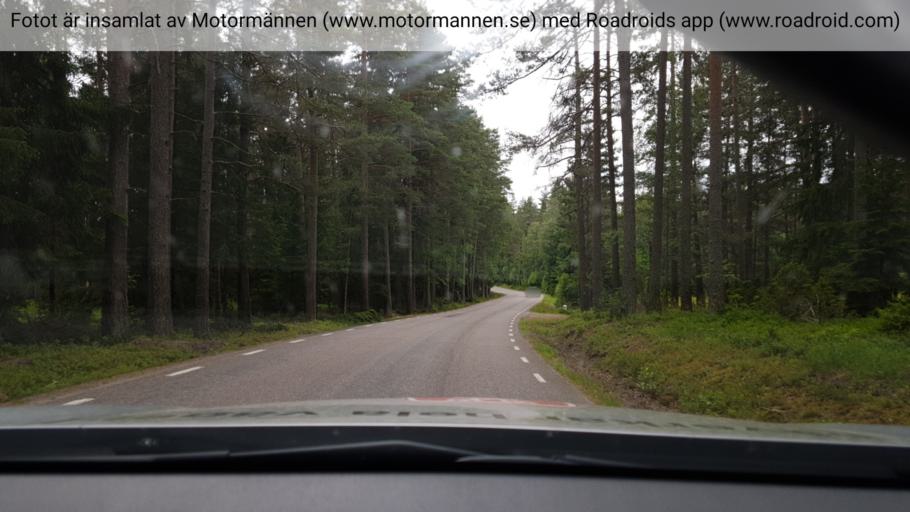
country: SE
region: Joenkoeping
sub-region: Habo Kommun
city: Habo
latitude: 58.0281
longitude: 14.0163
